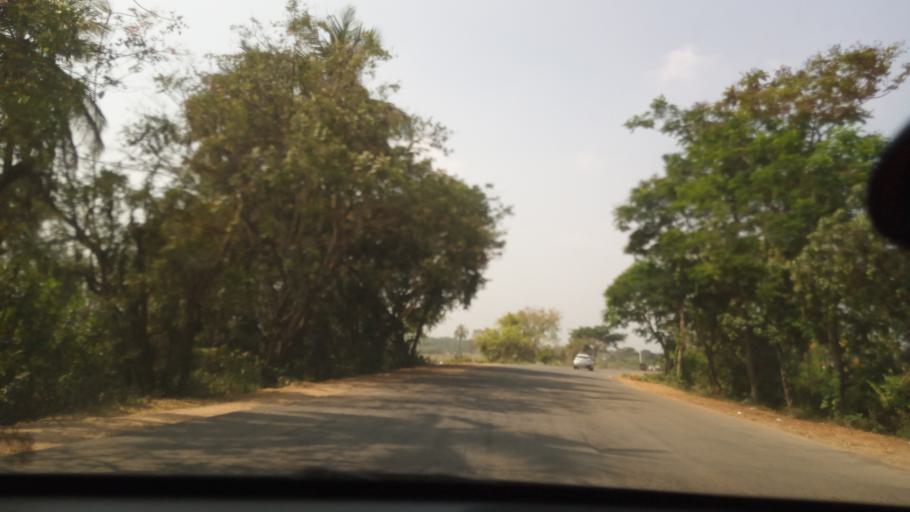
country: IN
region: Karnataka
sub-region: Mysore
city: Nanjangud
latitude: 12.1060
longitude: 76.7077
